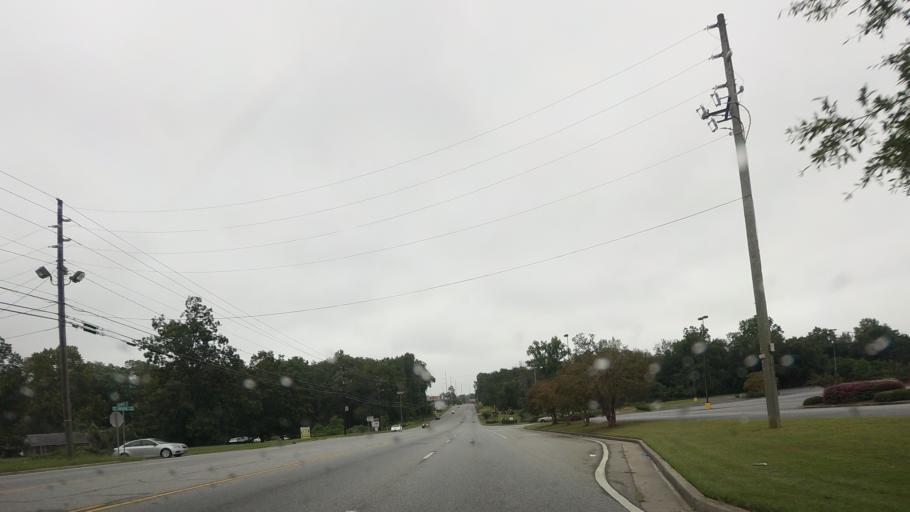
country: US
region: Georgia
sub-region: Lowndes County
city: Remerton
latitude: 30.8378
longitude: -83.3169
